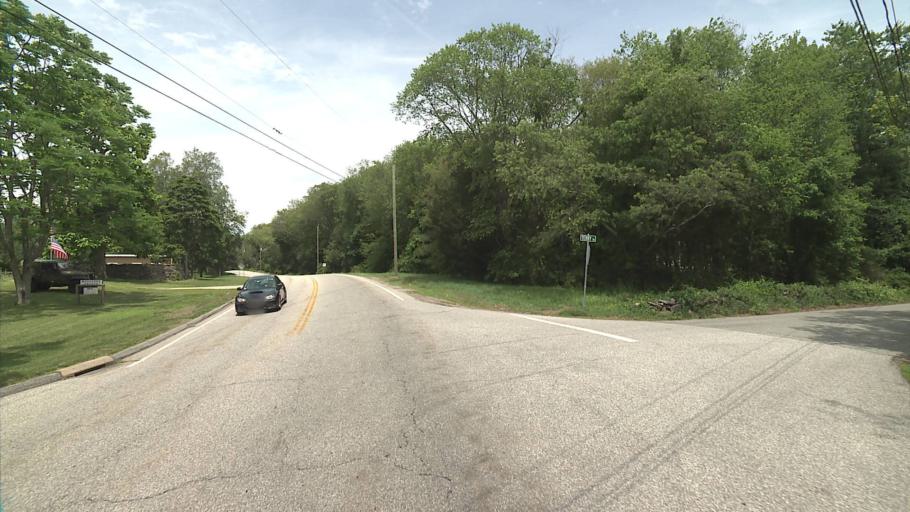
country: US
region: Connecticut
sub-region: New London County
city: Preston City
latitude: 41.5667
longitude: -71.9684
